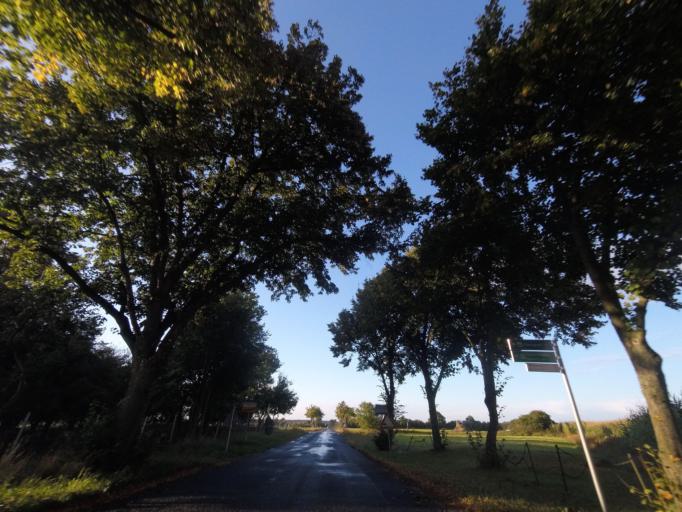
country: DE
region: Saxony-Anhalt
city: Kropstadt
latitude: 52.0159
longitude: 12.8197
